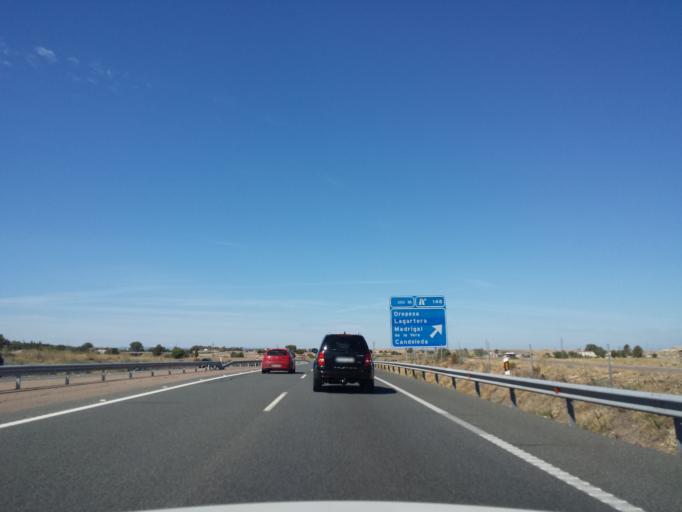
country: ES
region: Castille-La Mancha
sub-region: Province of Toledo
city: Oropesa
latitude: 39.9268
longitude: -5.1749
